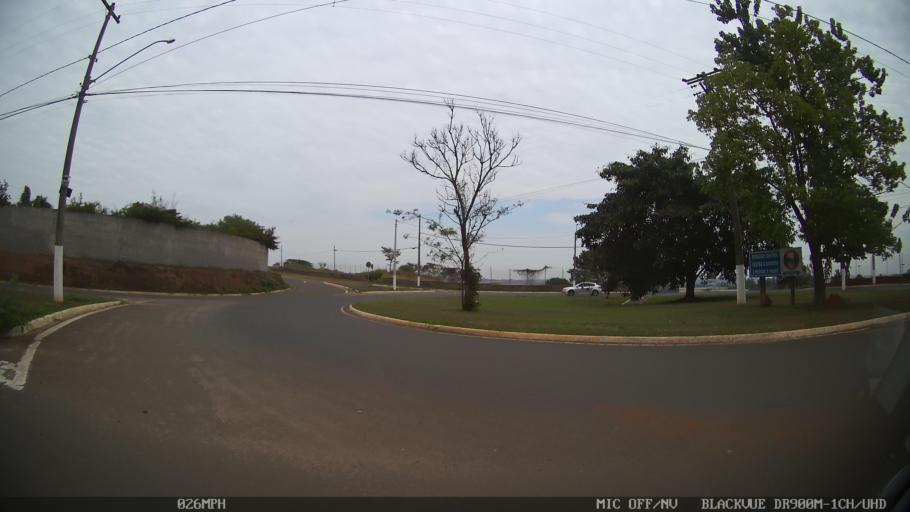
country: BR
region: Sao Paulo
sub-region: Paulinia
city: Paulinia
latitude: -22.7322
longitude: -47.1925
